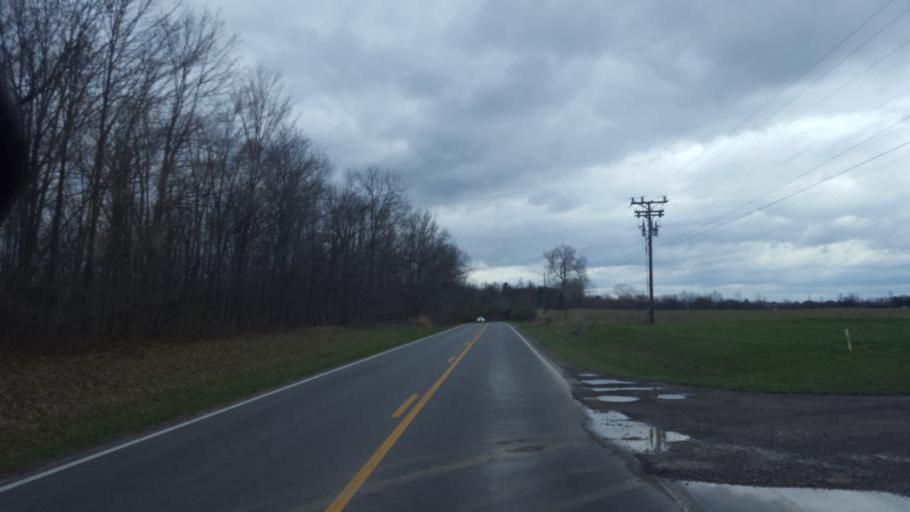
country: US
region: Ohio
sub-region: Delaware County
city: Sunbury
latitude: 40.2115
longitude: -82.8724
